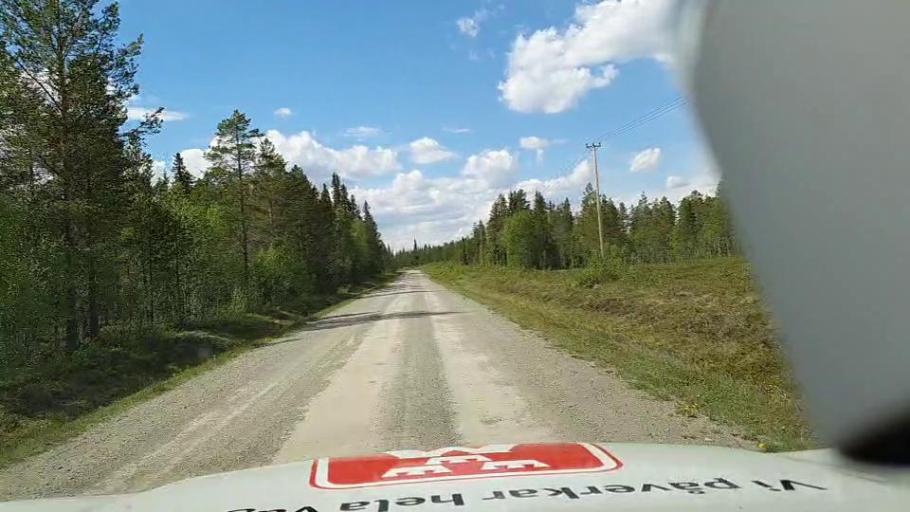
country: SE
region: Vaesterbotten
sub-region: Vilhelmina Kommun
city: Sjoberg
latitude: 64.5437
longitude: 15.6493
